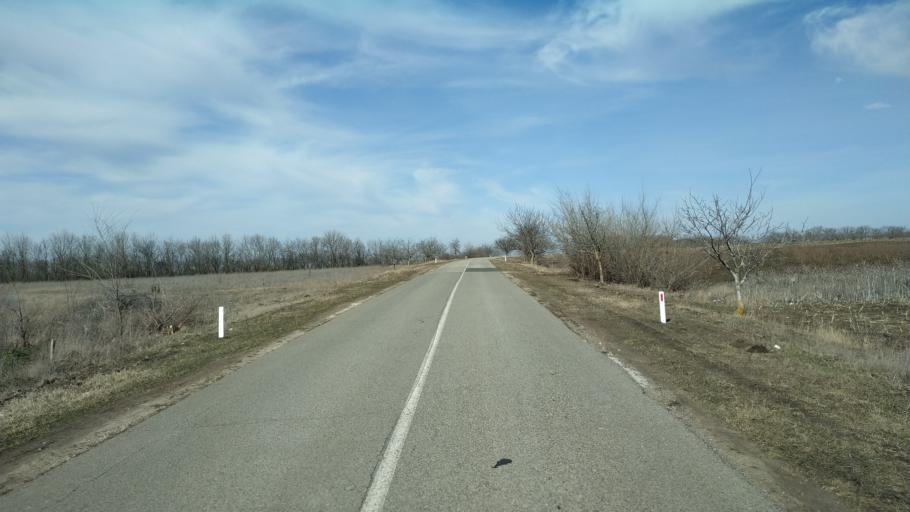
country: MD
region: Nisporeni
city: Nisporeni
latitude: 46.9425
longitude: 28.2431
